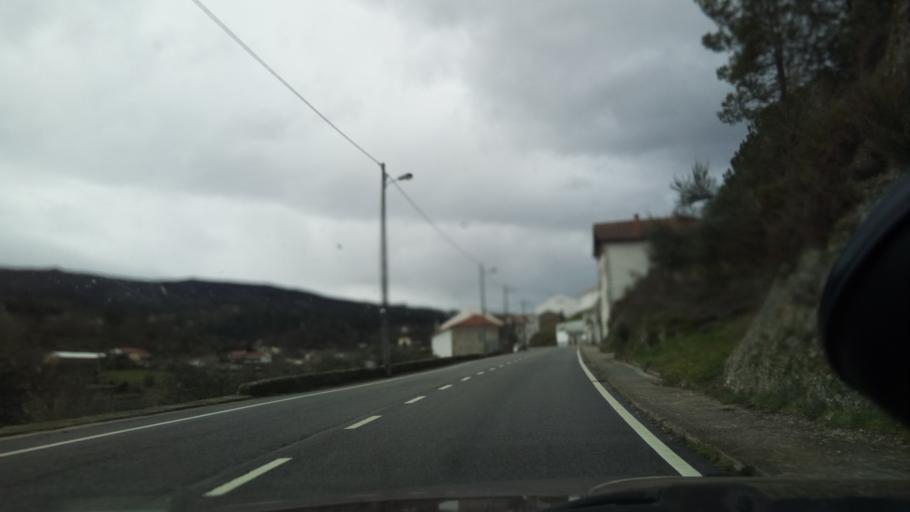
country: PT
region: Guarda
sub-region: Fornos de Algodres
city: Fornos de Algodres
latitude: 40.5197
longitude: -7.5803
